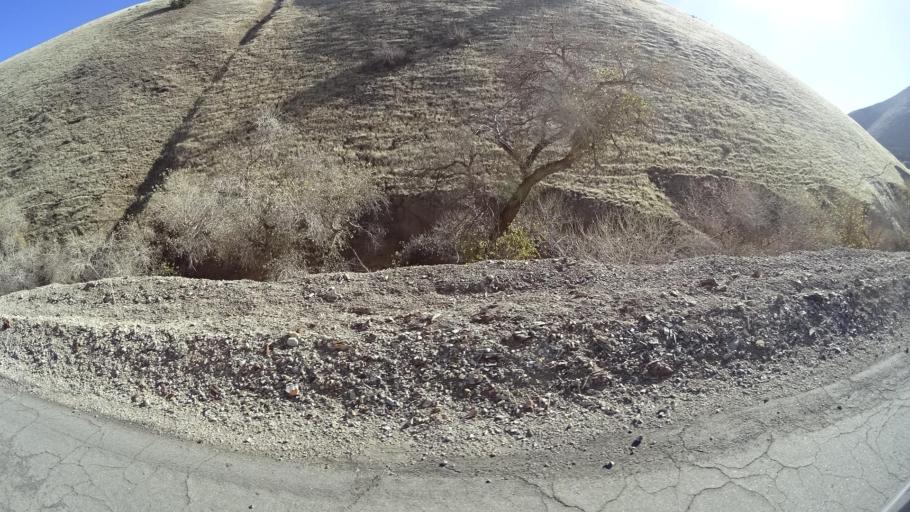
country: US
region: California
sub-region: Kern County
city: Maricopa
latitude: 34.9703
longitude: -119.4128
